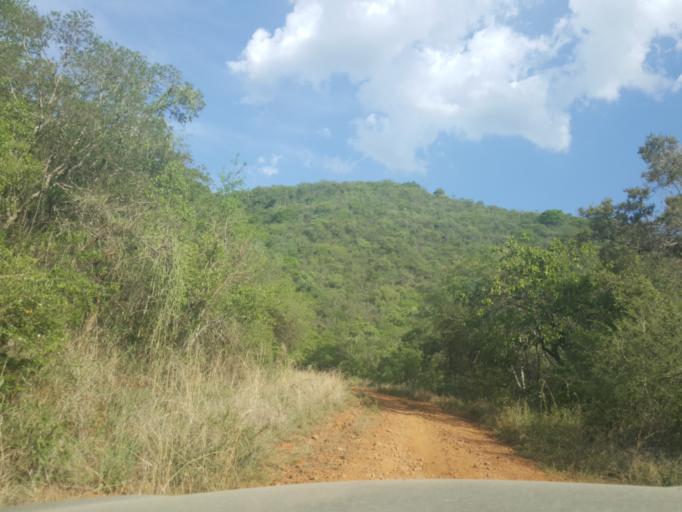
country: ZA
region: Limpopo
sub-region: Mopani District Municipality
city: Hoedspruit
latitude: -24.5902
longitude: 30.8291
